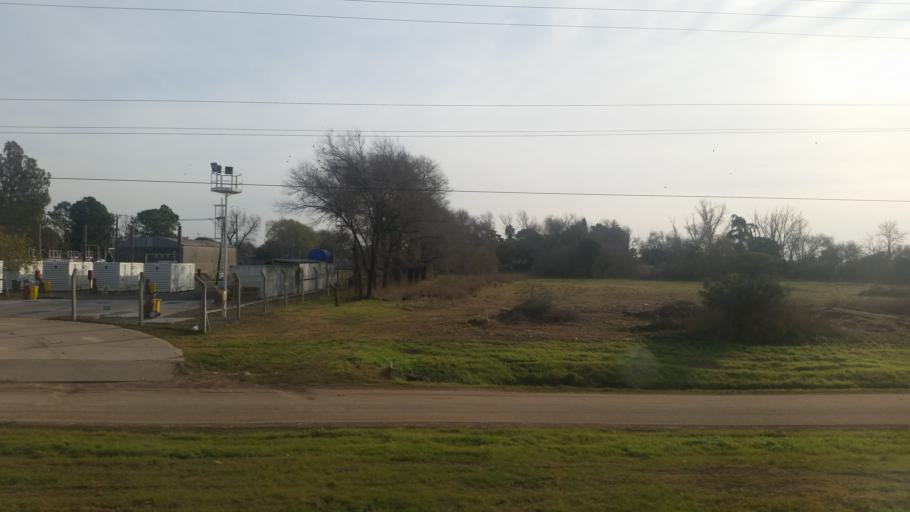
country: AR
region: Cordoba
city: Bell Ville
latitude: -32.6108
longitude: -62.6853
